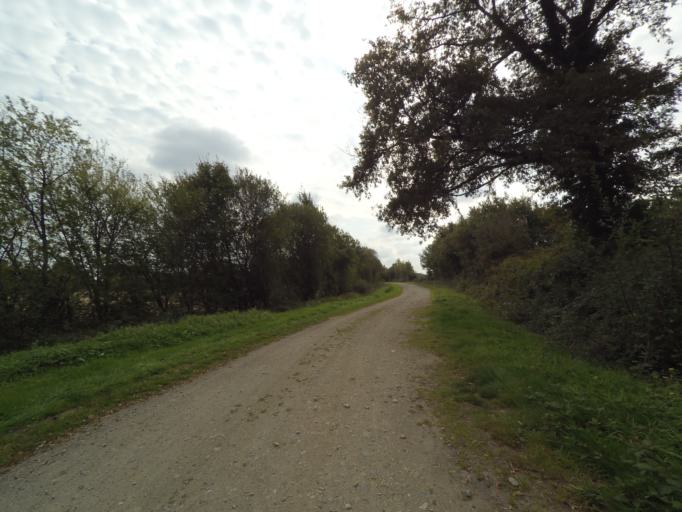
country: FR
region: Pays de la Loire
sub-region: Departement de la Vendee
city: Bouffere
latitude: 46.9774
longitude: -1.3519
